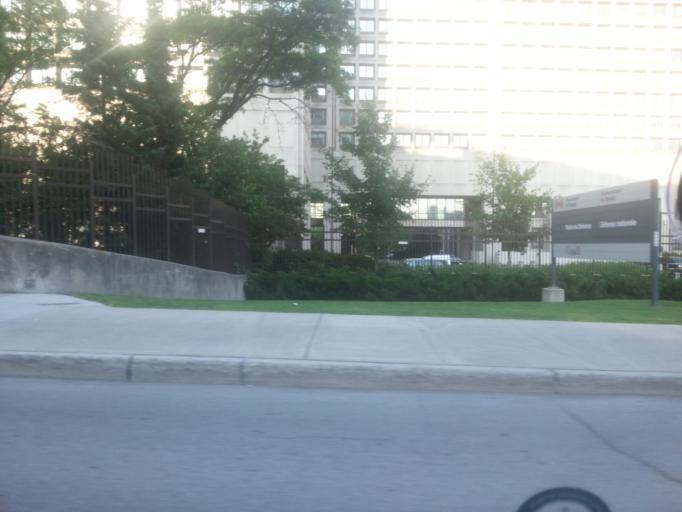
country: CA
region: Ontario
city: Ottawa
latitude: 45.4239
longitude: -75.6881
